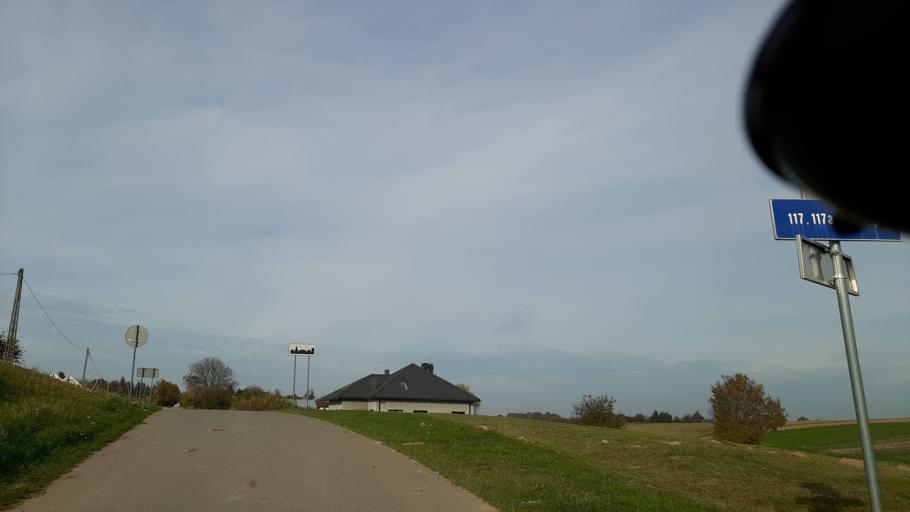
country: PL
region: Lublin Voivodeship
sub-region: Powiat lubelski
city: Jastkow
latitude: 51.3308
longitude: 22.4115
